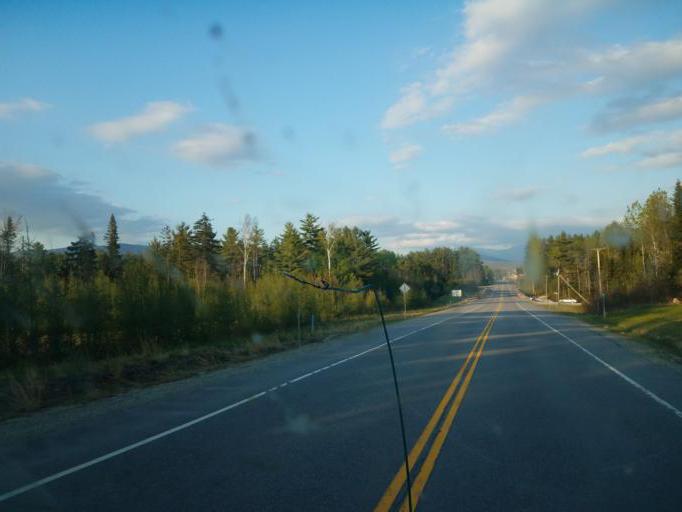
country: US
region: New Hampshire
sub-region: Grafton County
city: Deerfield
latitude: 44.2657
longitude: -71.5719
